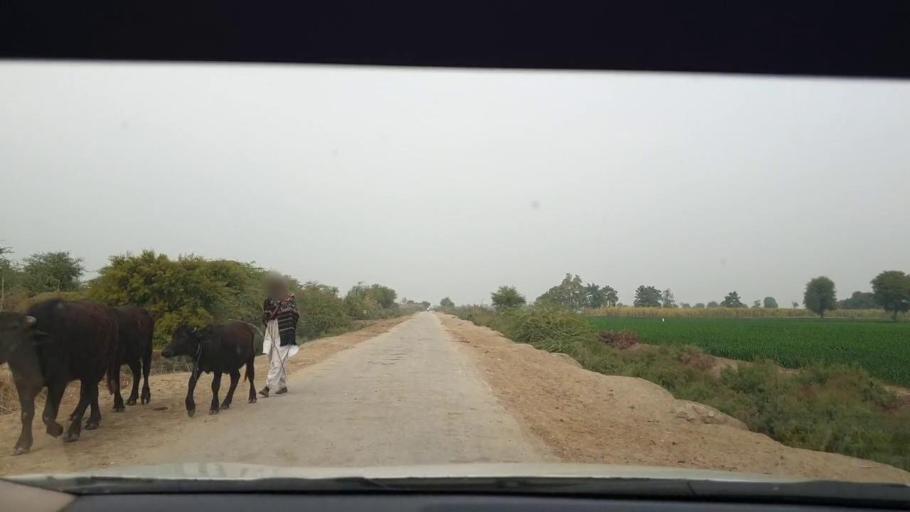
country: PK
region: Sindh
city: Berani
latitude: 25.8441
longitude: 68.8655
